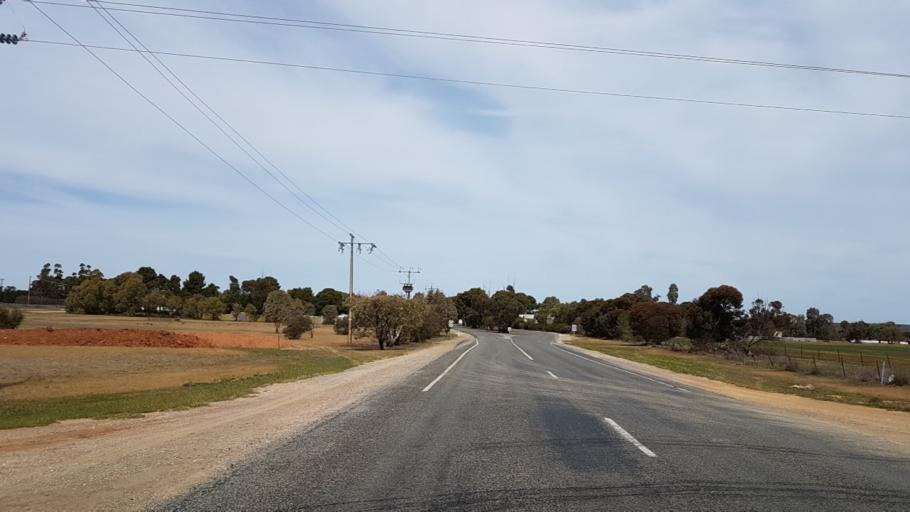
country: AU
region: South Australia
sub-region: Peterborough
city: Peterborough
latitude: -33.0250
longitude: 138.7501
